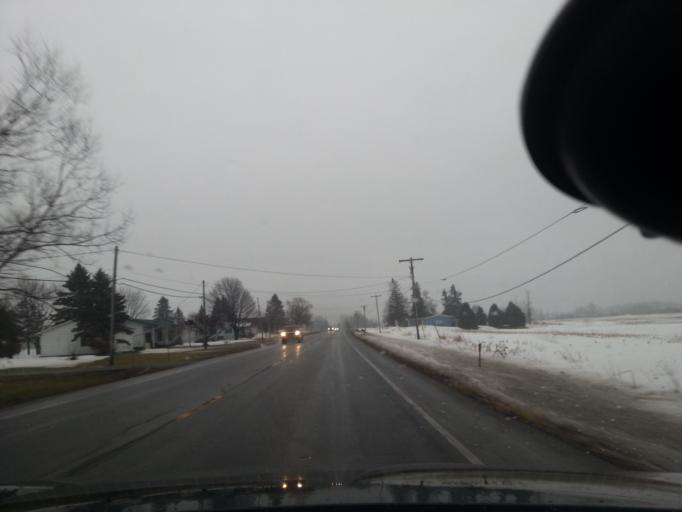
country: US
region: New York
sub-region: St. Lawrence County
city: Ogdensburg
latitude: 44.6757
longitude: -75.4753
